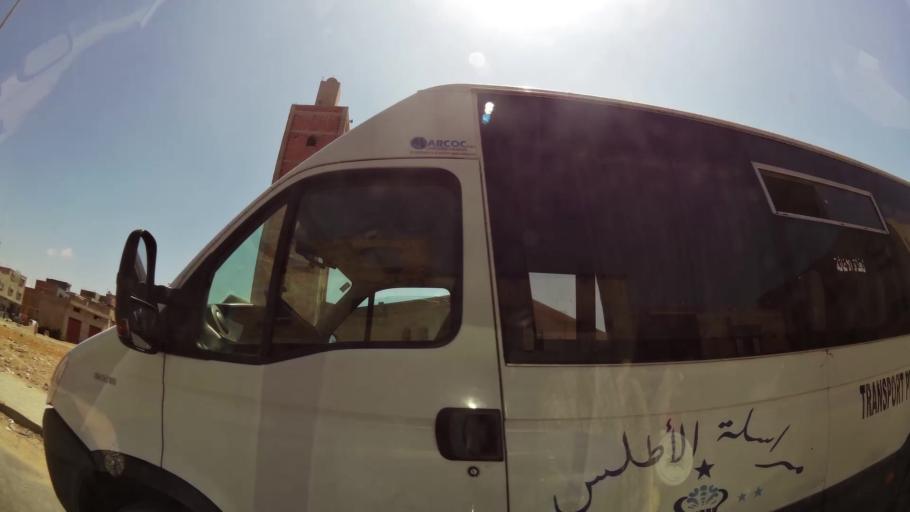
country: MA
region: Gharb-Chrarda-Beni Hssen
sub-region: Kenitra Province
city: Kenitra
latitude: 34.2286
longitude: -6.5439
